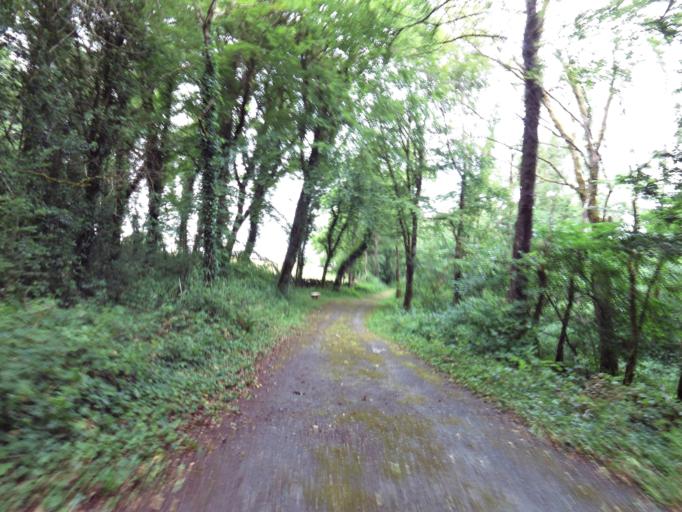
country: IE
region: Connaught
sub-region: County Galway
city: Gort
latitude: 53.0879
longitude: -8.8680
